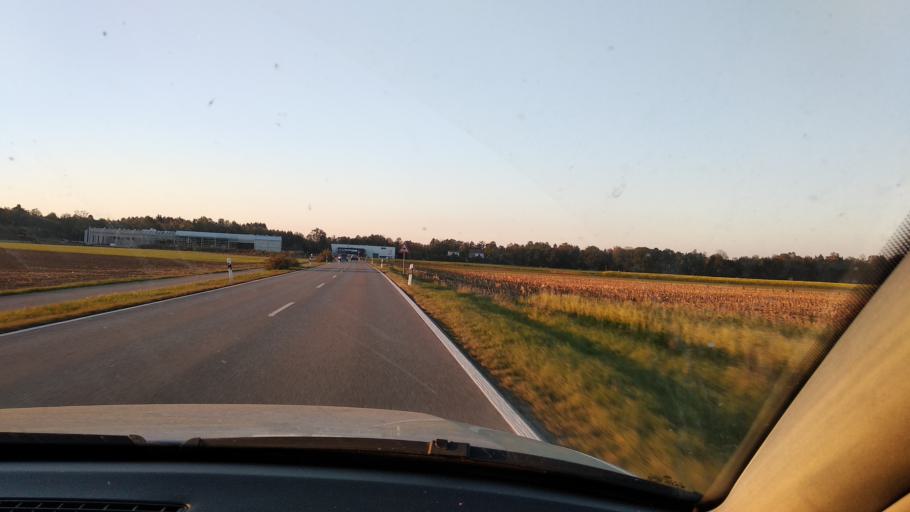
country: DE
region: Bavaria
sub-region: Upper Bavaria
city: Hohenkirchen-Siegertsbrunn
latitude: 48.0299
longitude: 11.7204
